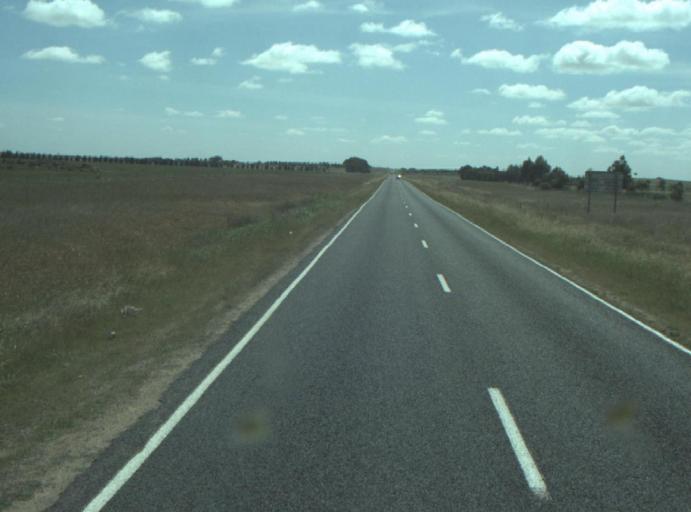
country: AU
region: Victoria
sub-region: Wyndham
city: Little River
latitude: -38.0068
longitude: 144.4638
